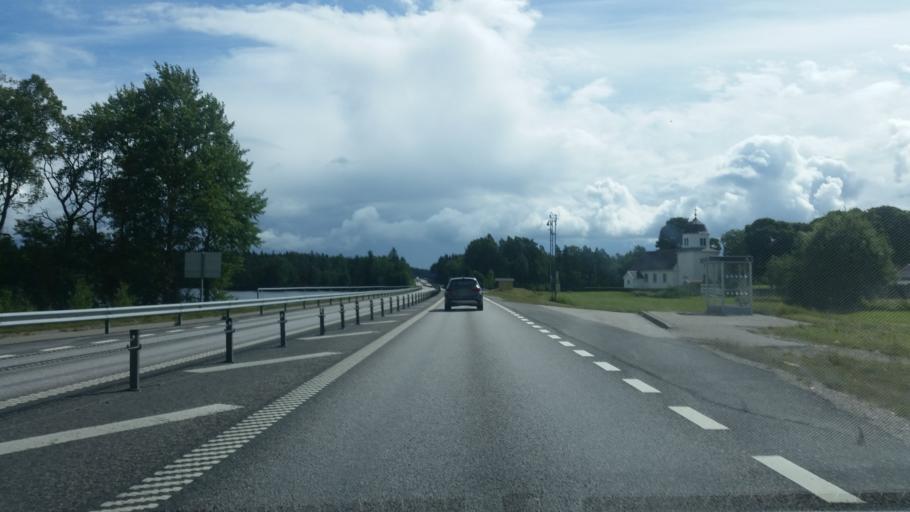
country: SE
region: Joenkoeping
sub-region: Mullsjo Kommun
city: Mullsjoe
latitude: 57.7764
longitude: 13.6752
